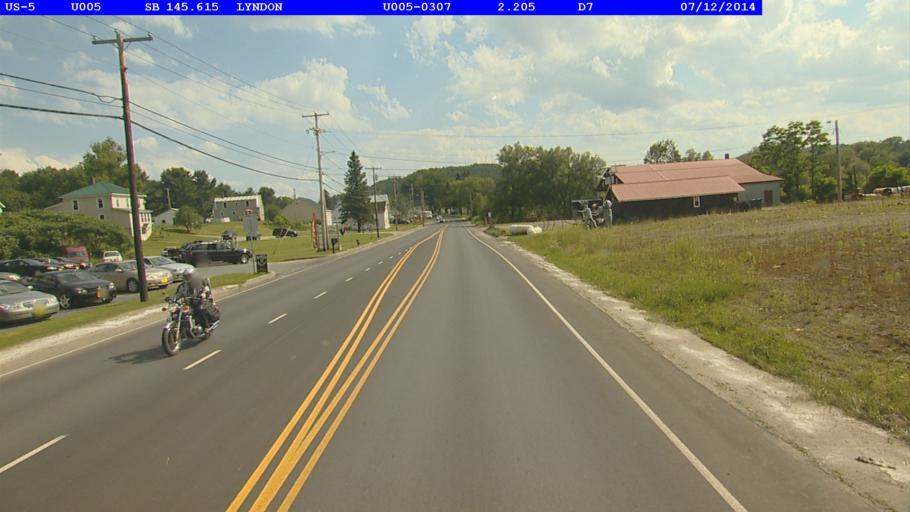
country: US
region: Vermont
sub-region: Caledonia County
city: Lyndonville
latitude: 44.5252
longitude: -72.0010
